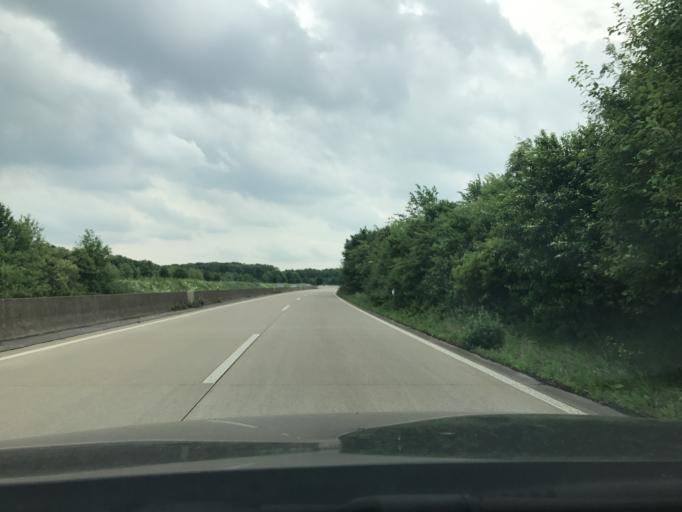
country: DE
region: North Rhine-Westphalia
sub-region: Regierungsbezirk Dusseldorf
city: Ratingen
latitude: 51.3111
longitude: 6.7733
